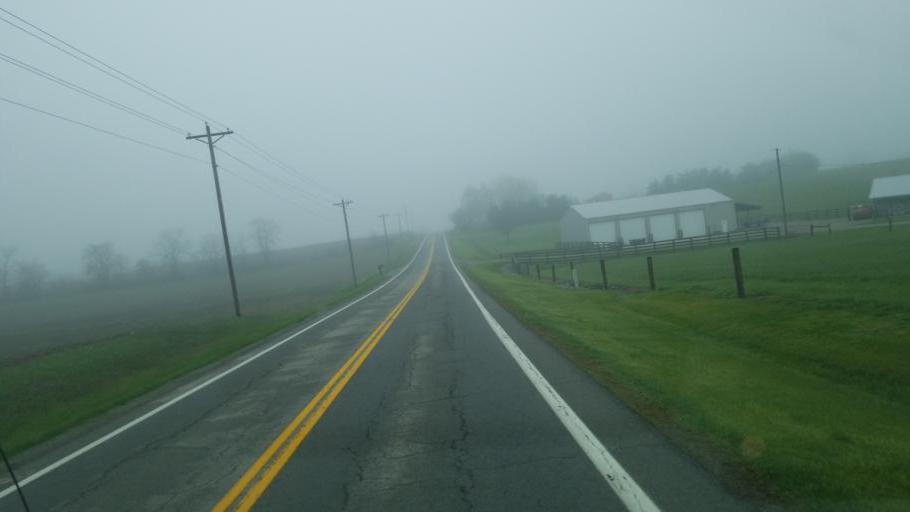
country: US
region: Ohio
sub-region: Logan County
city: Northwood
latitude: 40.4203
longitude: -83.6000
